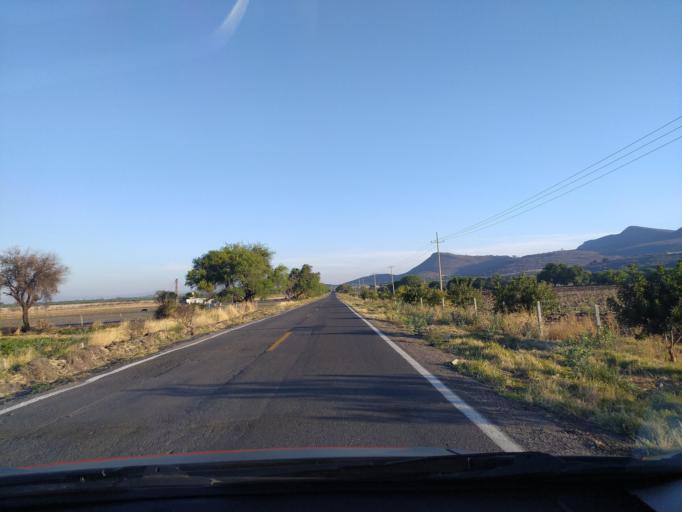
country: MX
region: Guanajuato
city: Ciudad Manuel Doblado
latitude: 20.7675
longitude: -101.8298
